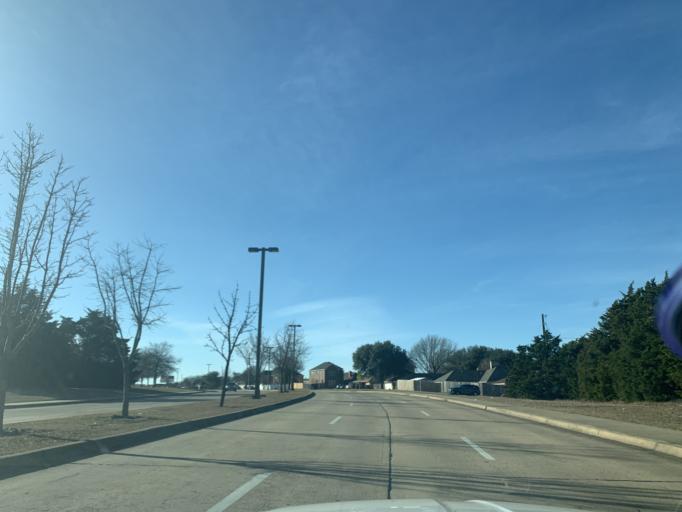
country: US
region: Texas
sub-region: Dallas County
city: DeSoto
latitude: 32.5880
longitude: -96.8393
